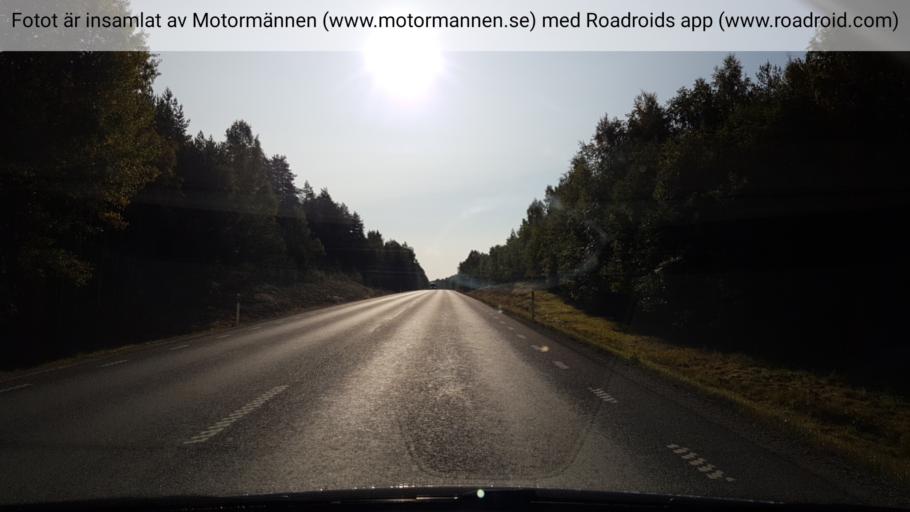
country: SE
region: Vaesterbotten
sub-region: Umea Kommun
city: Roback
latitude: 63.8533
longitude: 20.1044
